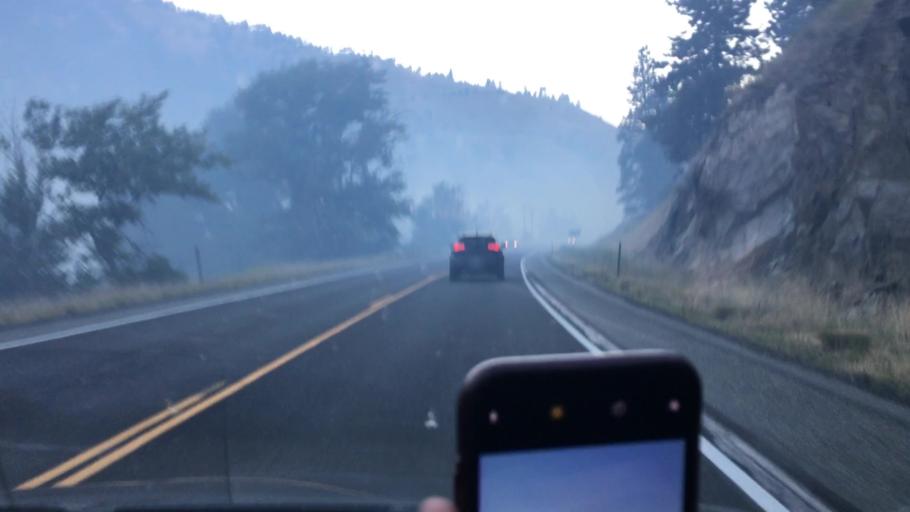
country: US
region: Idaho
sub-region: Valley County
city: McCall
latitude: 45.2857
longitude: -116.3523
